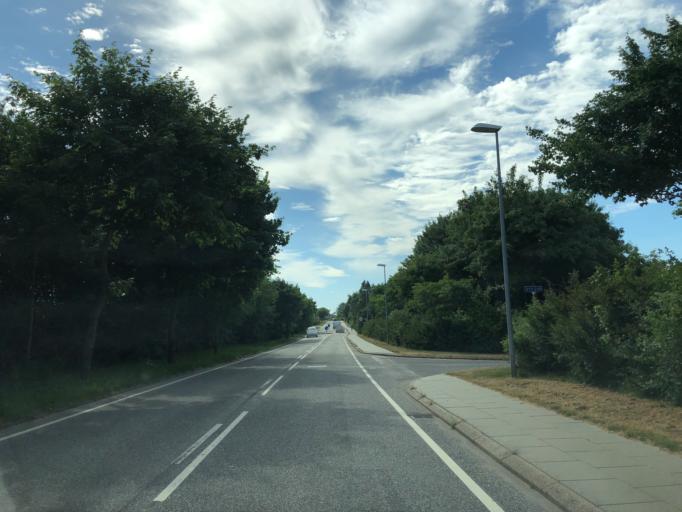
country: DK
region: Central Jutland
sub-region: Herning Kommune
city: Snejbjerg
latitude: 56.1258
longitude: 8.9017
